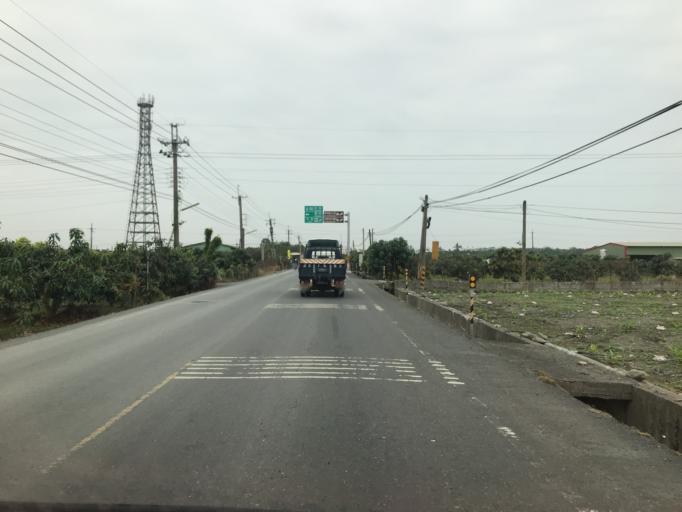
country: TW
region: Taiwan
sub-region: Pingtung
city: Pingtung
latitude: 22.5015
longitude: 120.5887
